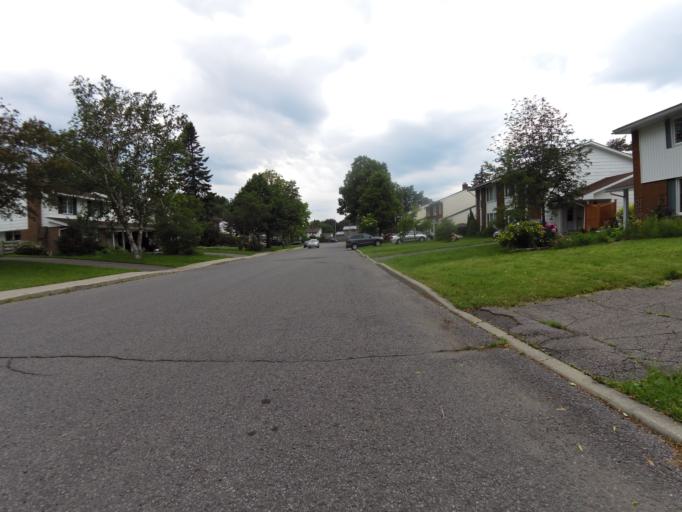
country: CA
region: Ontario
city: Bells Corners
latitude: 45.3380
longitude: -75.7844
